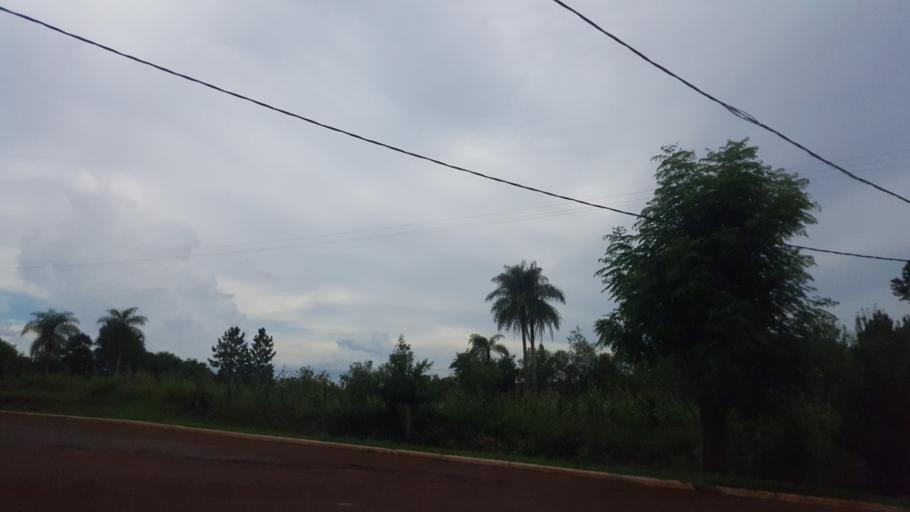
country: AR
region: Misiones
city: Santo Pipo
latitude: -27.1075
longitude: -55.3784
